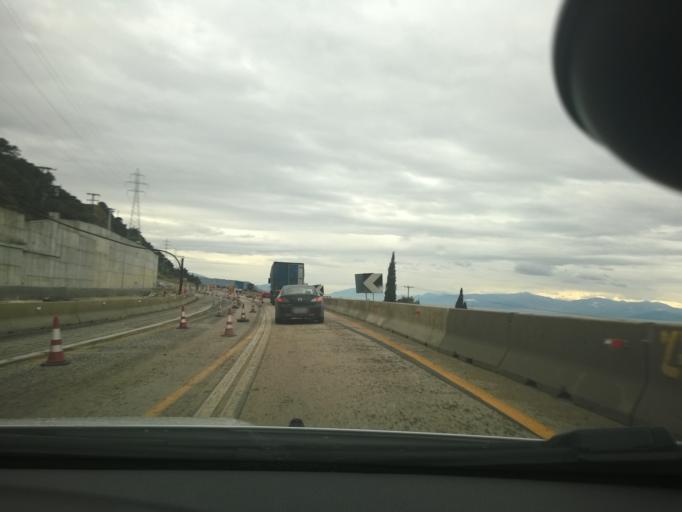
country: GR
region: West Greece
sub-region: Nomos Achaias
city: Aiyira
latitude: 38.1310
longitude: 22.4443
